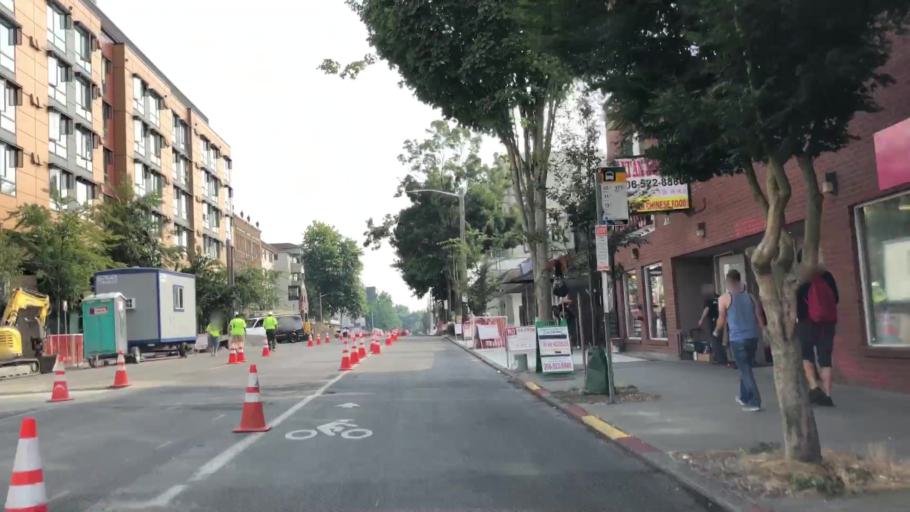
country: US
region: Washington
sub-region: King County
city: Seattle
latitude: 47.6684
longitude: -122.3130
